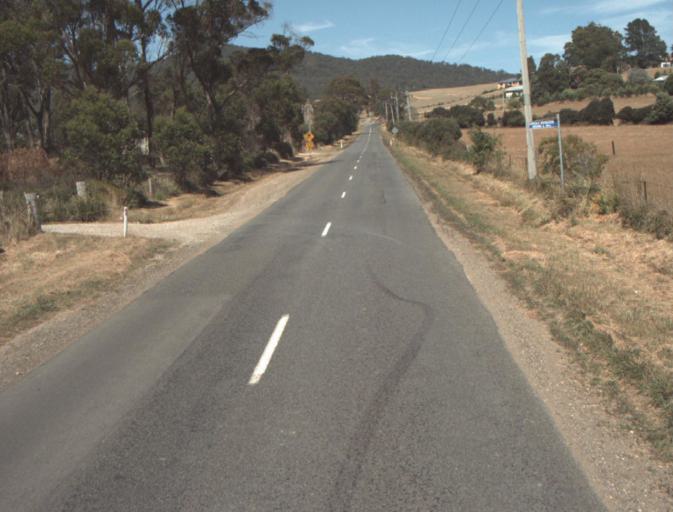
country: AU
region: Tasmania
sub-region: Launceston
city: Mayfield
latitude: -41.2542
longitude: 147.1469
